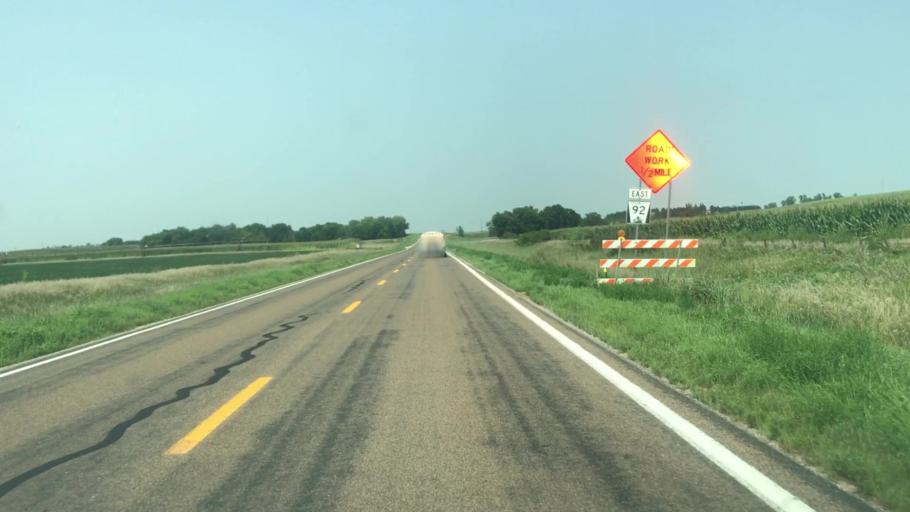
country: US
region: Nebraska
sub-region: Sherman County
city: Loup City
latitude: 41.2554
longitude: -98.9389
